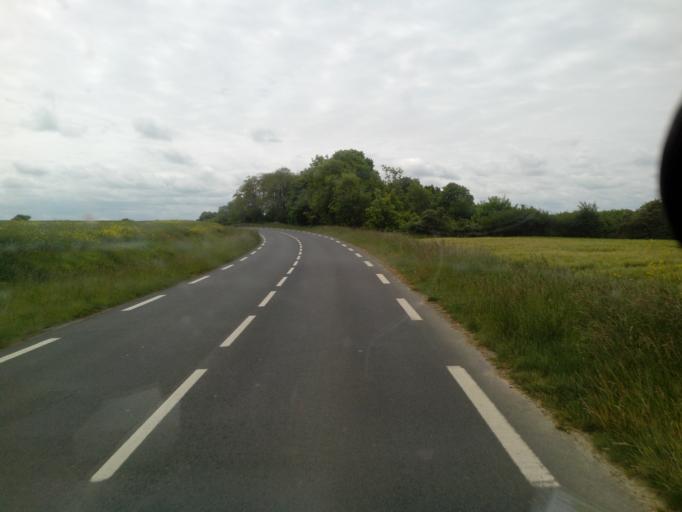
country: FR
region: Lower Normandy
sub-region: Departement du Calvados
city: Amfreville
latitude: 49.2553
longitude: -0.2411
